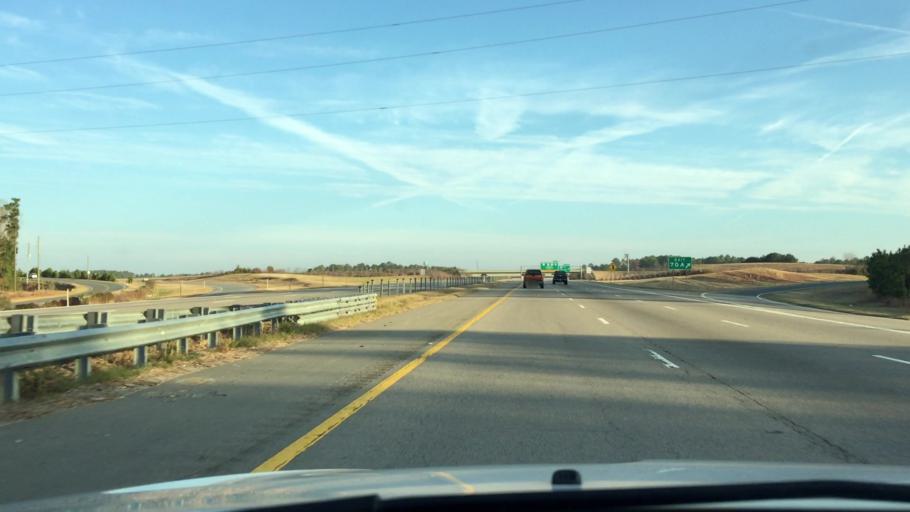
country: US
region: North Carolina
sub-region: Lee County
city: Sanford
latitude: 35.5065
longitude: -79.1895
